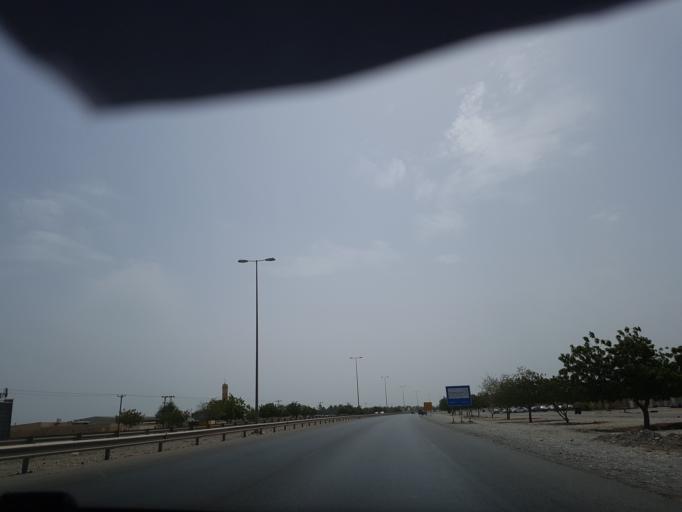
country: OM
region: Al Batinah
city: As Suwayq
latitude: 23.7562
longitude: 57.6004
